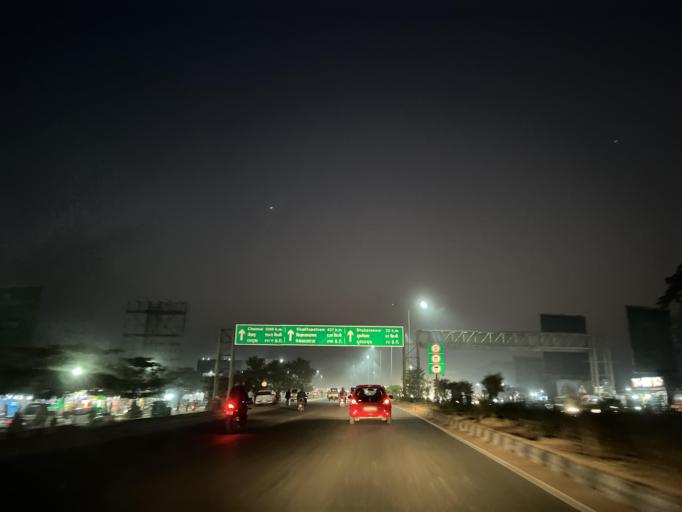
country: IN
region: Odisha
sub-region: Cuttack
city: Cuttack
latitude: 20.4358
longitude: 85.8841
